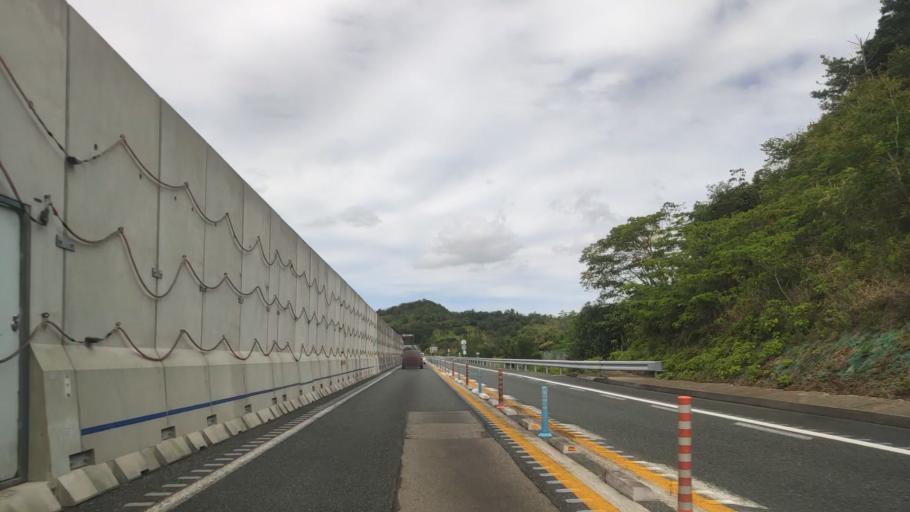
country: JP
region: Wakayama
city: Gobo
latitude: 33.8722
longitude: 135.1885
